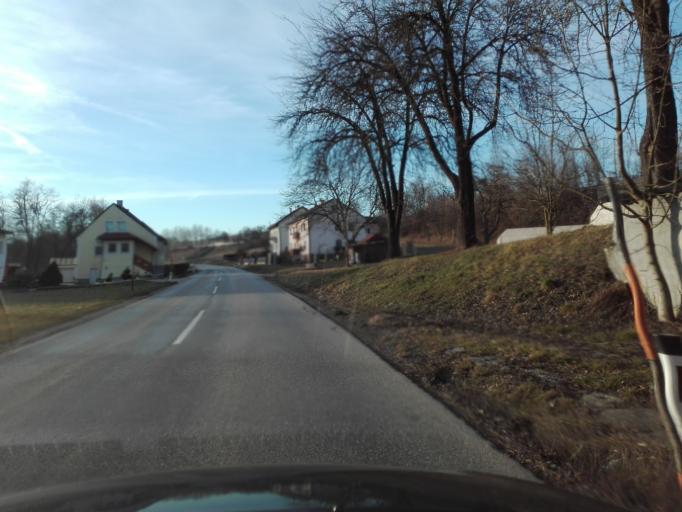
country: AT
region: Lower Austria
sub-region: Politischer Bezirk Amstetten
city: Haag
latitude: 48.1156
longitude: 14.5513
